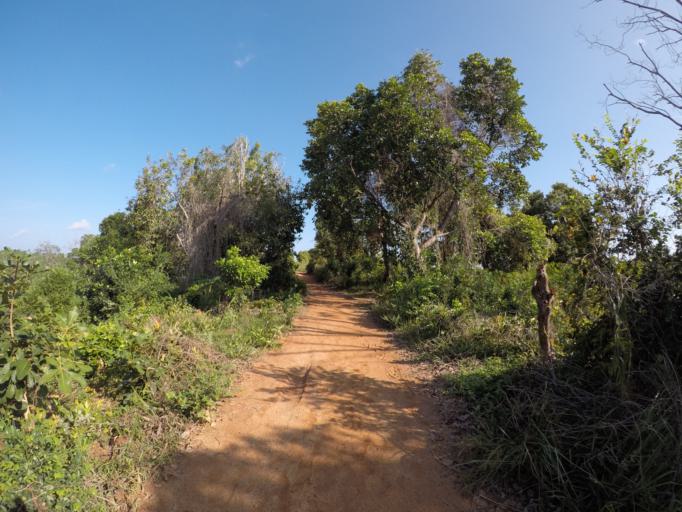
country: TZ
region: Pemba South
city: Mtambile
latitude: -5.3892
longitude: 39.7288
